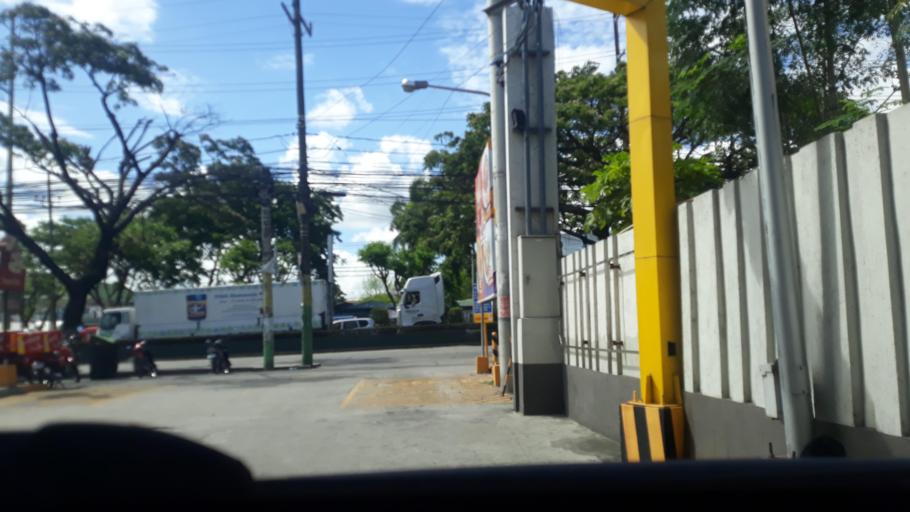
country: PH
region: Calabarzon
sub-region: Province of Cavite
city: Manggahan
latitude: 14.2923
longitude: 120.9321
